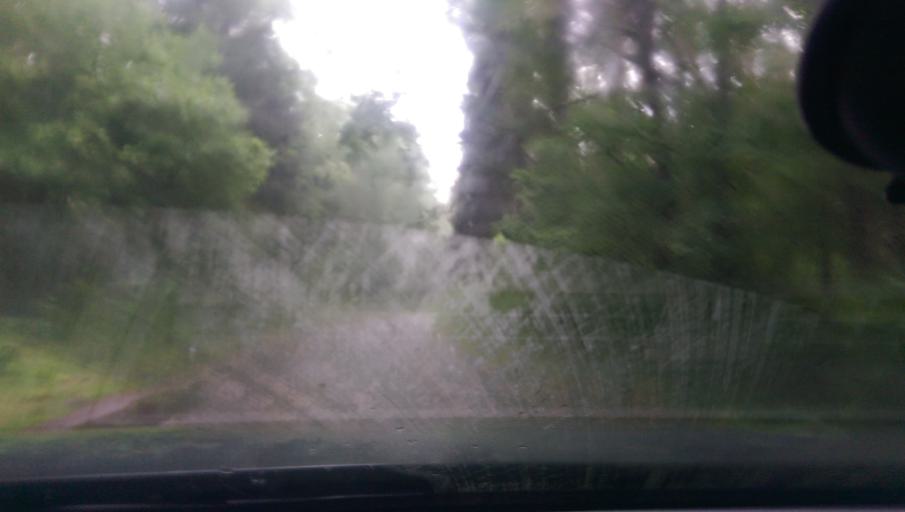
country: PL
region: Warmian-Masurian Voivodeship
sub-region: Powiat mragowski
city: Piecki
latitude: 53.7602
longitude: 21.4277
